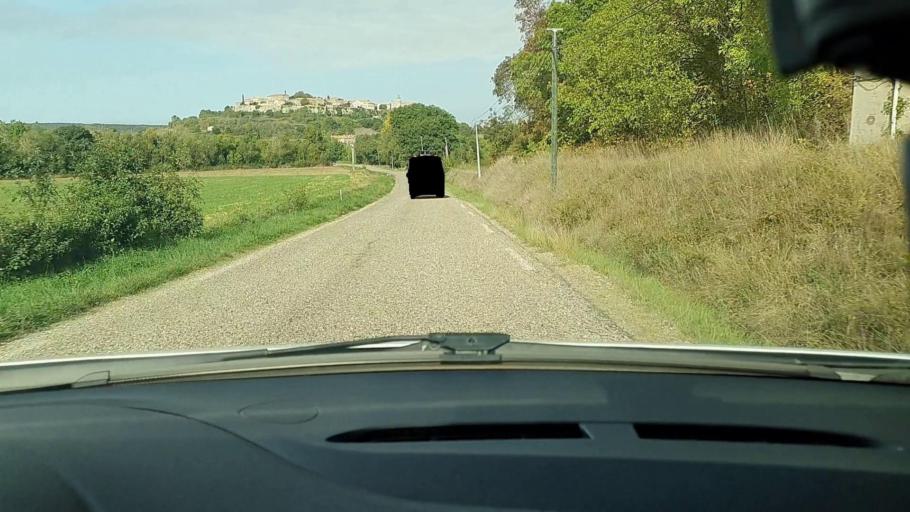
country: FR
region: Languedoc-Roussillon
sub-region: Departement du Gard
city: Goudargues
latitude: 44.1482
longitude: 4.3768
